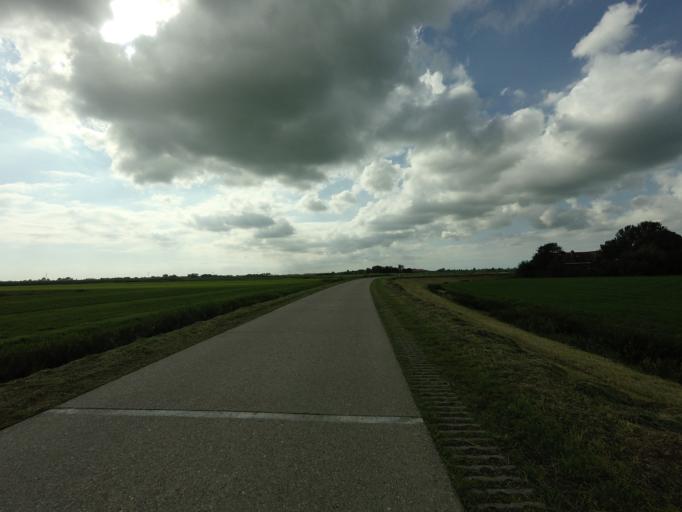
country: NL
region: Friesland
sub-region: Gemeente Littenseradiel
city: Wommels
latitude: 53.0747
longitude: 5.6199
